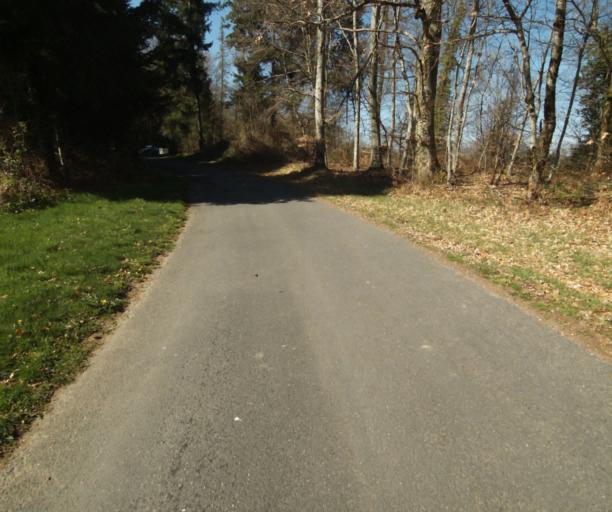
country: FR
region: Limousin
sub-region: Departement de la Correze
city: Saint-Mexant
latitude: 45.2921
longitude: 1.7008
